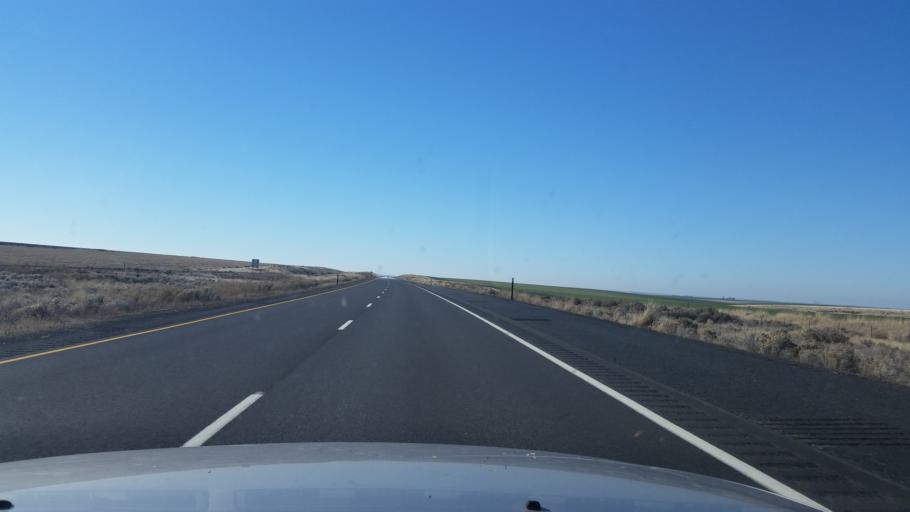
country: US
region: Washington
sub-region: Adams County
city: Ritzville
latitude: 47.0954
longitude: -118.6900
